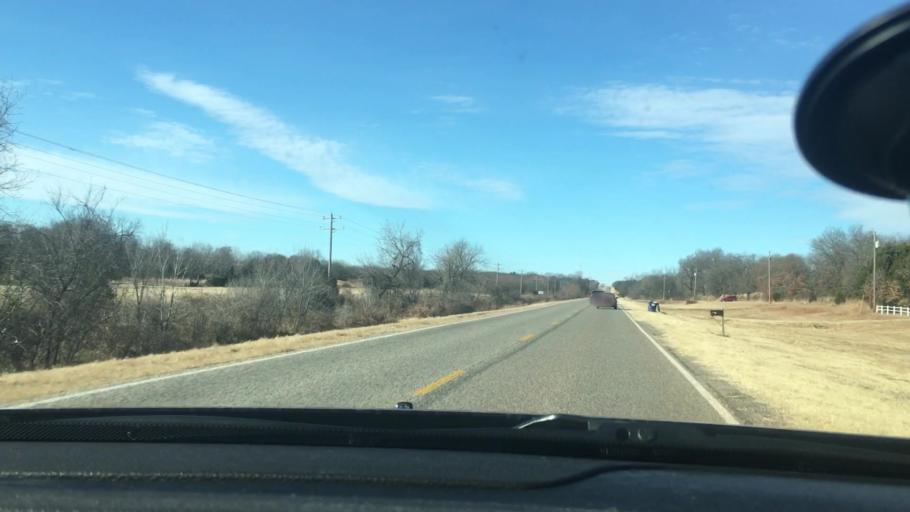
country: US
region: Oklahoma
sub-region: Cleveland County
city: Lexington
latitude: 35.0149
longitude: -97.1517
